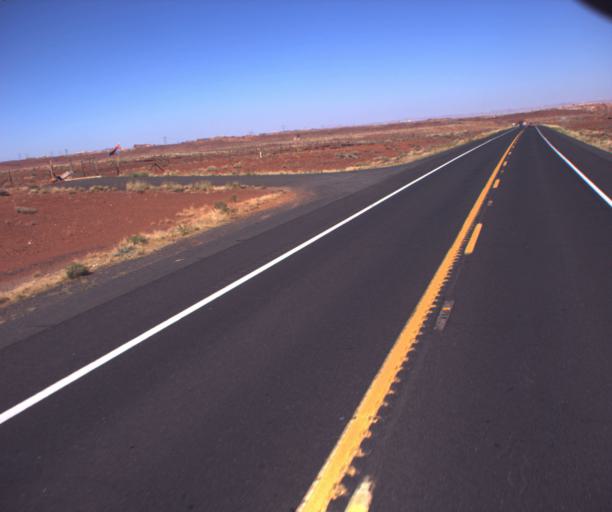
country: US
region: Arizona
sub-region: Coconino County
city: Tuba City
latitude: 35.7798
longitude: -111.4579
